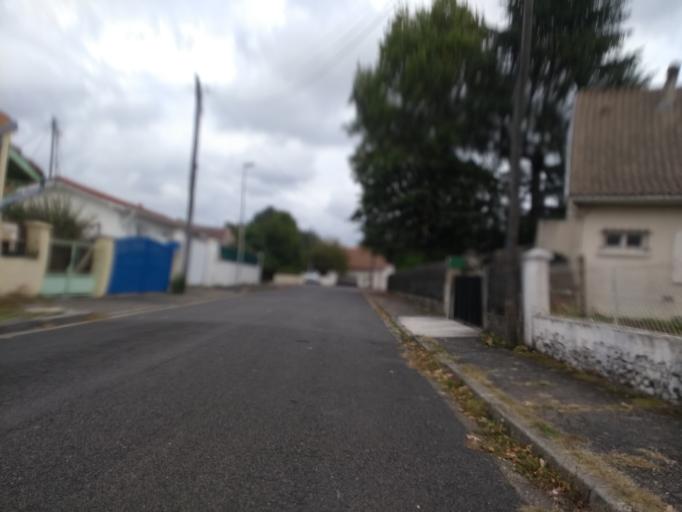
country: FR
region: Aquitaine
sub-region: Departement de la Gironde
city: Pessac
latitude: 44.7942
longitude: -0.6444
